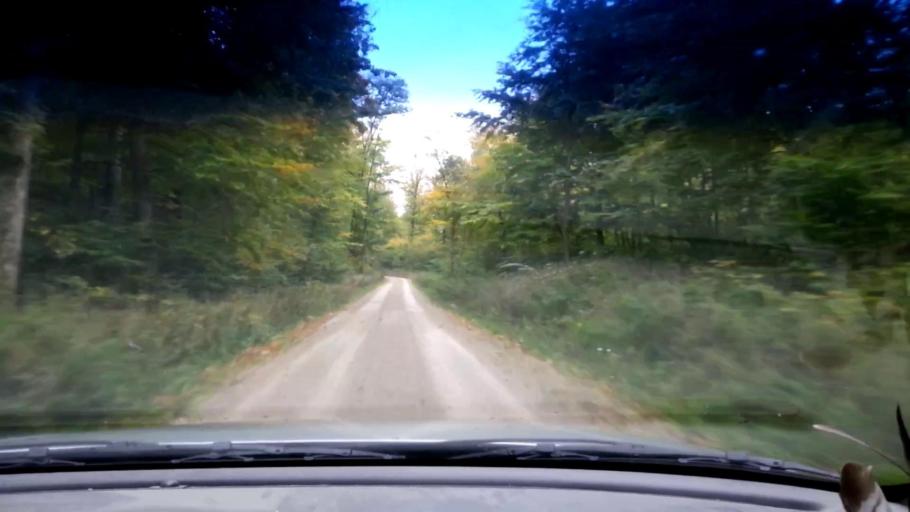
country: DE
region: Bavaria
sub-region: Upper Franconia
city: Litzendorf
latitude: 49.8974
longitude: 11.0596
